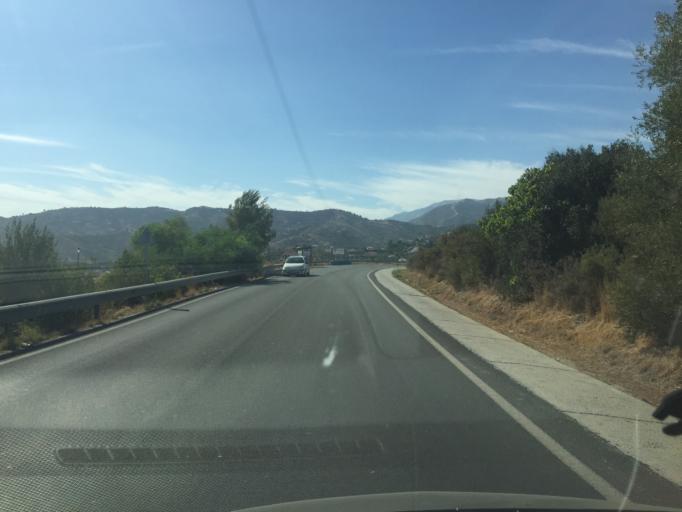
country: ES
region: Andalusia
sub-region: Provincia de Malaga
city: Frigiliana
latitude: 36.7759
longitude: -3.8959
